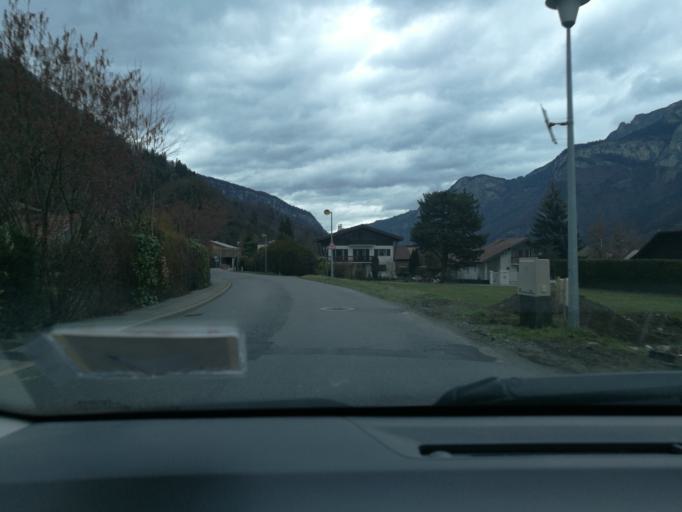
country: FR
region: Rhone-Alpes
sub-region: Departement de la Haute-Savoie
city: Sallanches
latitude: 45.9475
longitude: 6.6277
